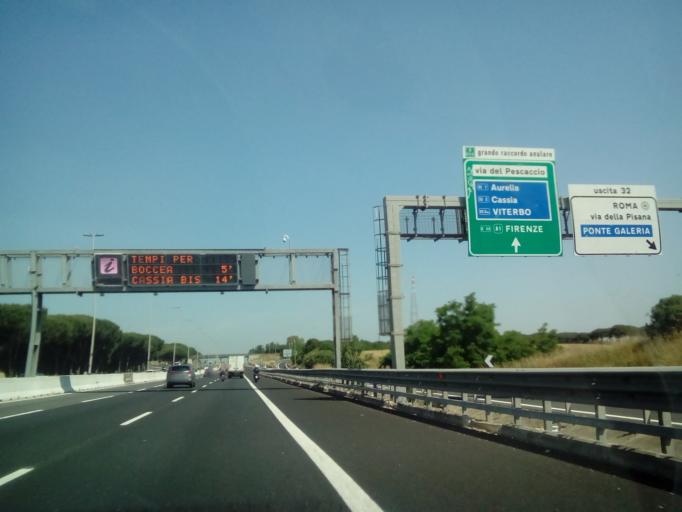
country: IT
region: Latium
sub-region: Citta metropolitana di Roma Capitale
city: La Massimina-Casal Lumbroso
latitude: 41.8466
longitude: 12.3814
